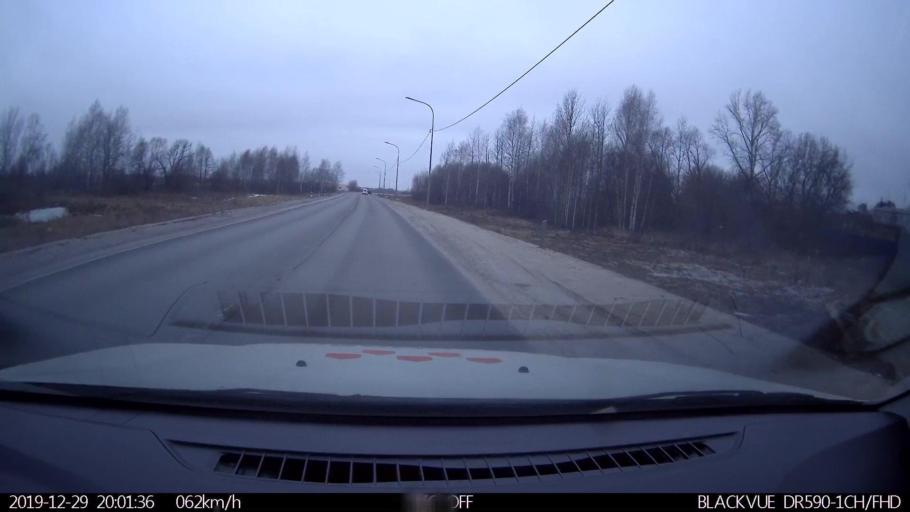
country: RU
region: Nizjnij Novgorod
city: Bor
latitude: 56.3601
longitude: 44.0413
